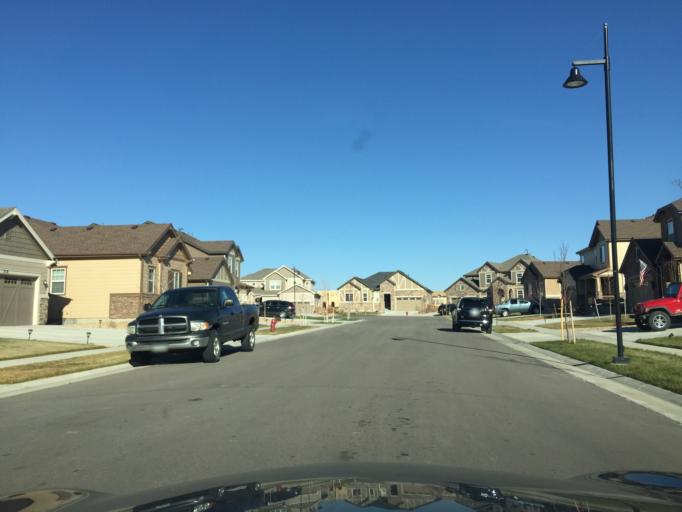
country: US
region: Colorado
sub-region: Boulder County
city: Erie
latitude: 40.0465
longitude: -105.0313
